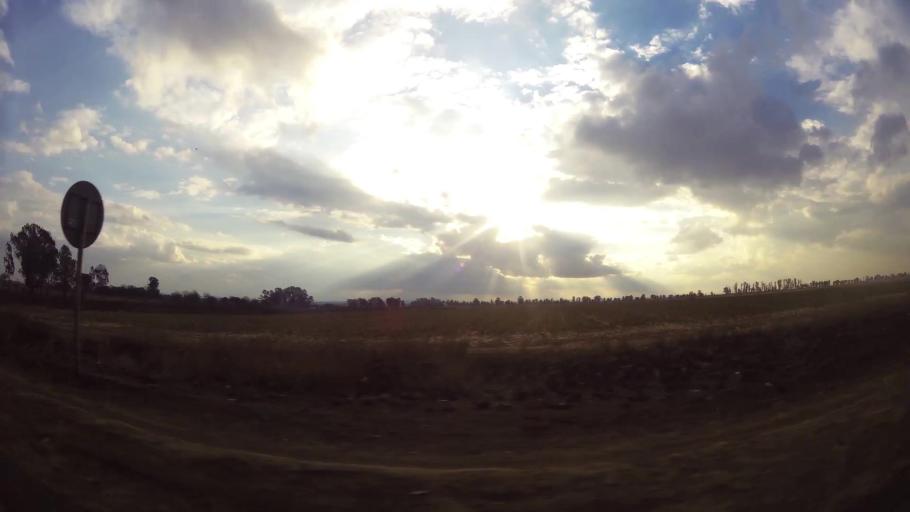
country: ZA
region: Gauteng
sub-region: Sedibeng District Municipality
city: Vanderbijlpark
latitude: -26.6605
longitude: 27.7994
